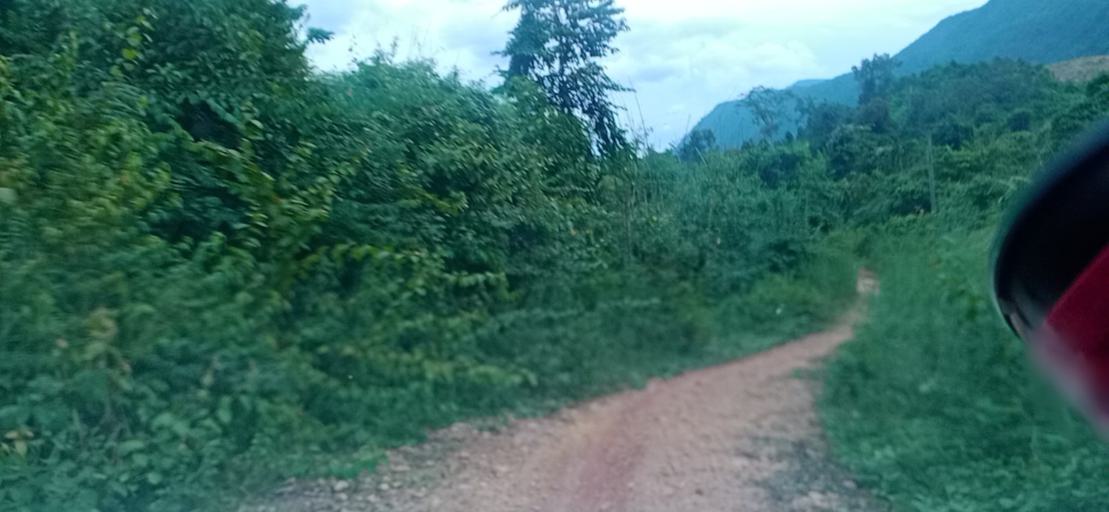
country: TH
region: Changwat Bueng Kan
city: Pak Khat
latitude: 18.5631
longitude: 103.2751
